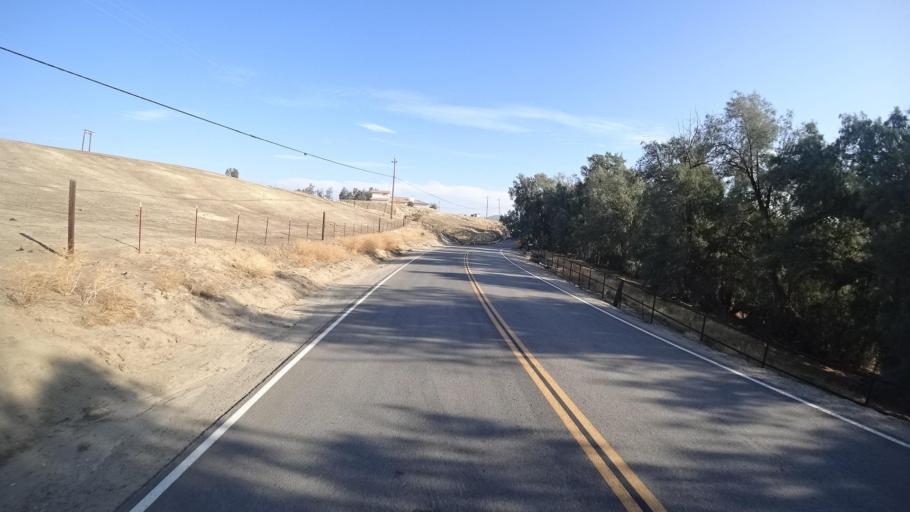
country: US
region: California
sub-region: Kern County
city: Oildale
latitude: 35.4388
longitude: -118.8936
